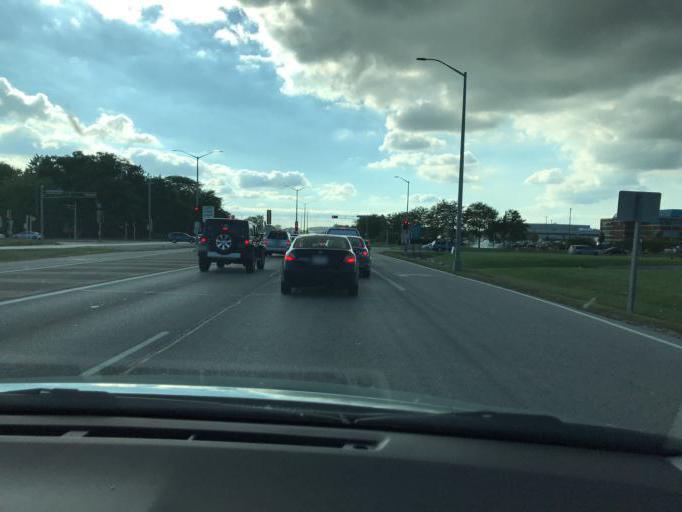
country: US
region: Wisconsin
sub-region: Kenosha County
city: Pleasant Prairie
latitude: 42.5673
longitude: -87.9325
